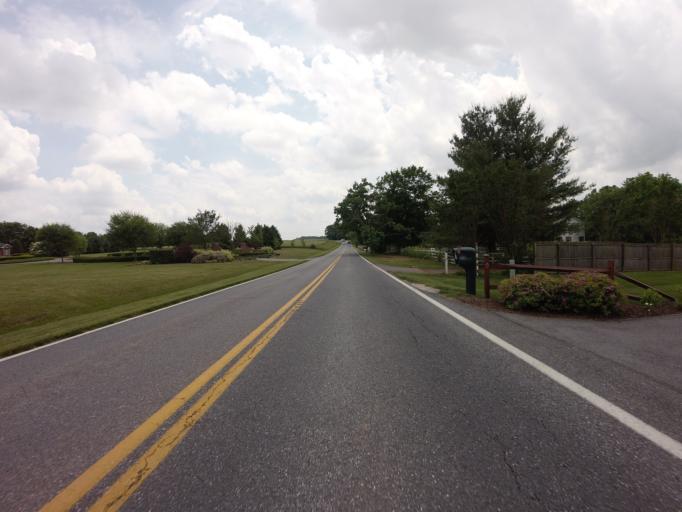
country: US
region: Maryland
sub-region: Frederick County
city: Ballenger Creek
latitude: 39.3758
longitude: -77.4593
